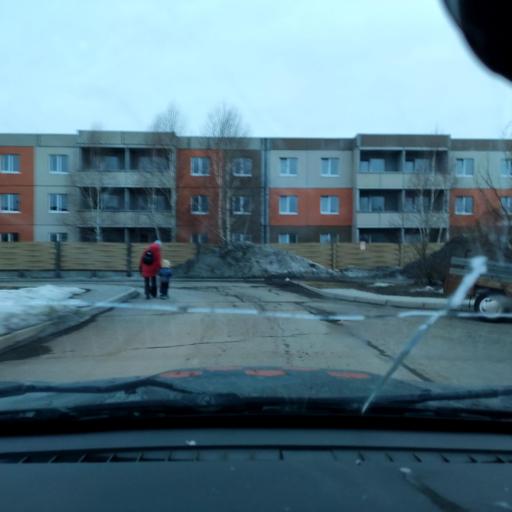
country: RU
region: Samara
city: Tol'yatti
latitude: 53.6196
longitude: 49.3148
